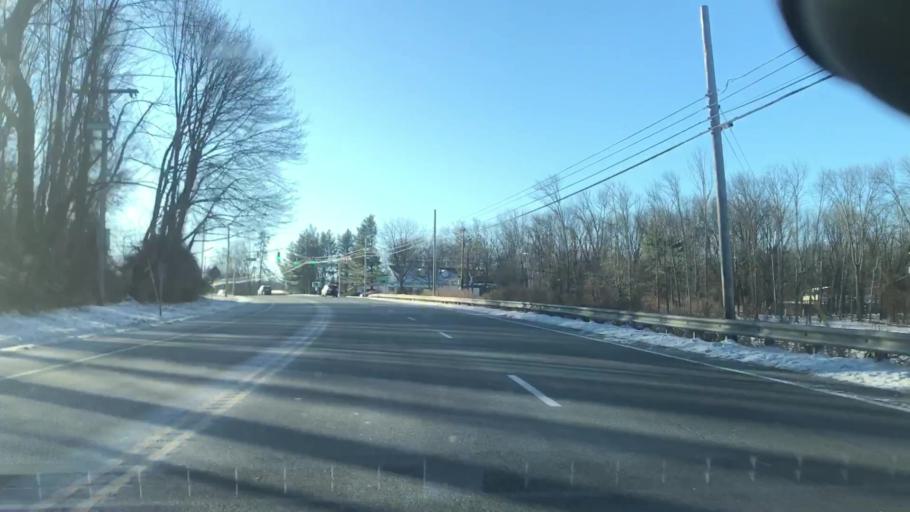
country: US
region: New Jersey
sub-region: Morris County
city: Chester
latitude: 40.8045
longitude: -74.7147
